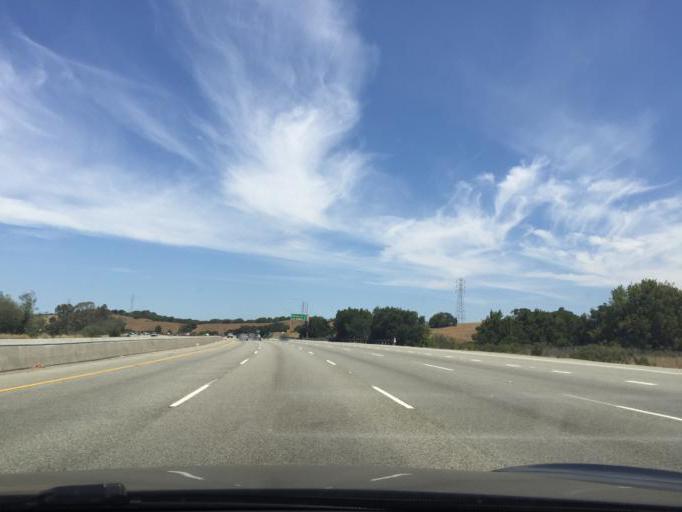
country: US
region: California
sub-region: San Mateo County
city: Emerald Lake Hills
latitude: 37.4643
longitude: -122.2908
